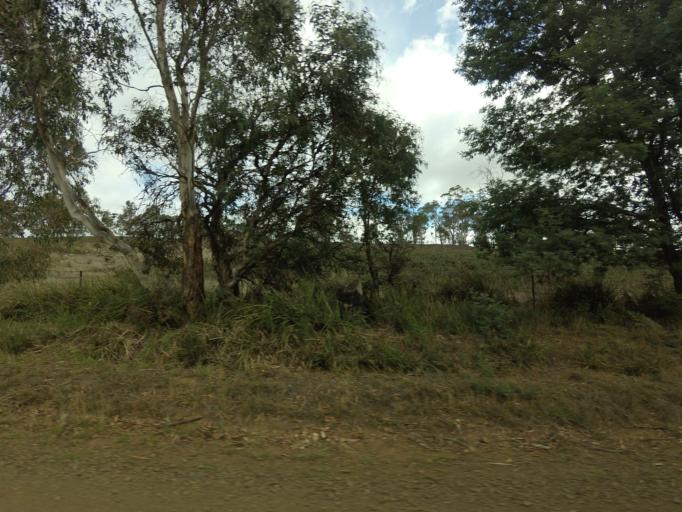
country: AU
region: Tasmania
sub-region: Brighton
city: Bridgewater
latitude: -42.4782
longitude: 147.2931
